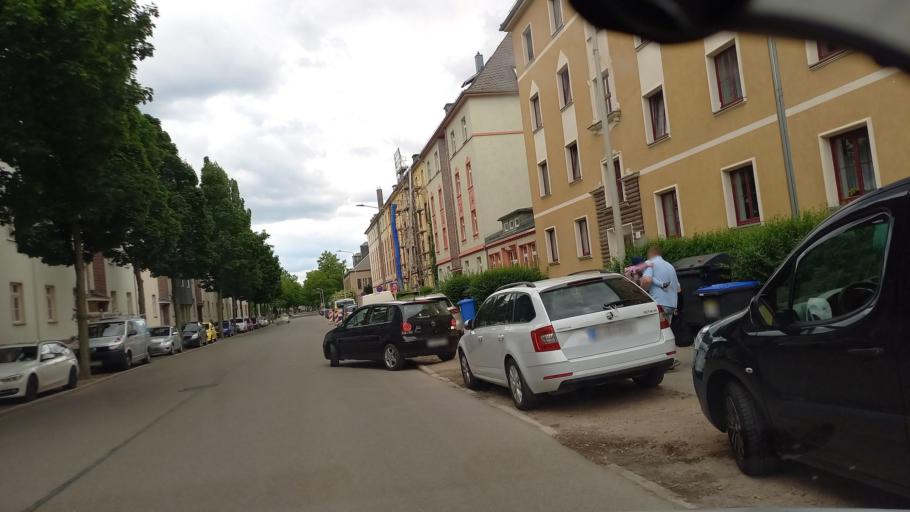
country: DE
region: Saxony
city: Zwickau
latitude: 50.7375
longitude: 12.4878
